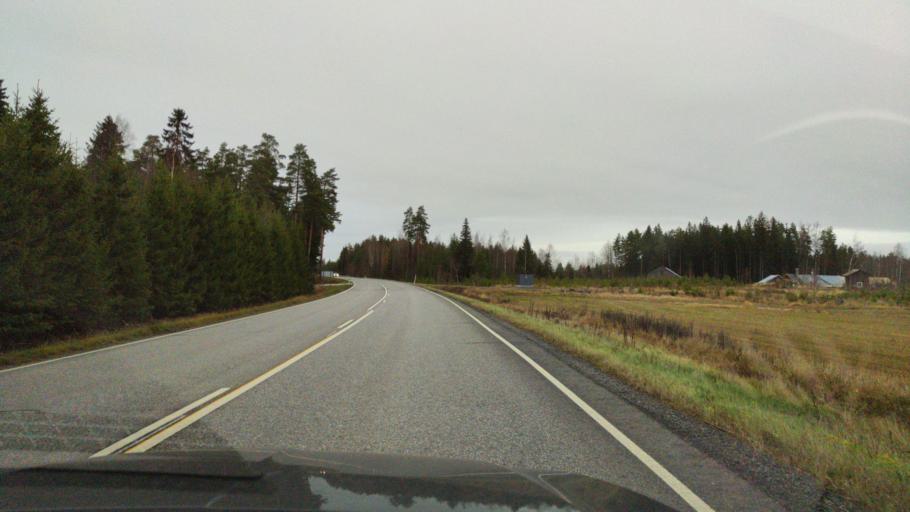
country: FI
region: Varsinais-Suomi
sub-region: Turku
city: Lieto
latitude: 60.5992
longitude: 22.4260
